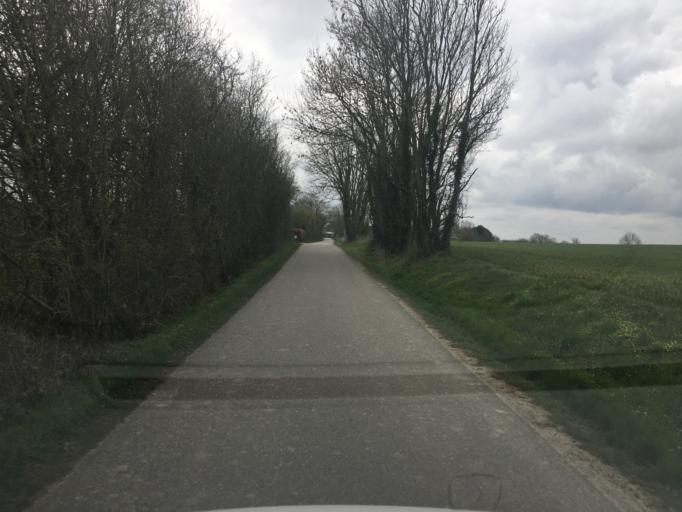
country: DK
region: South Denmark
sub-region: Sonderborg Kommune
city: Grasten
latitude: 54.8951
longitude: 9.5497
